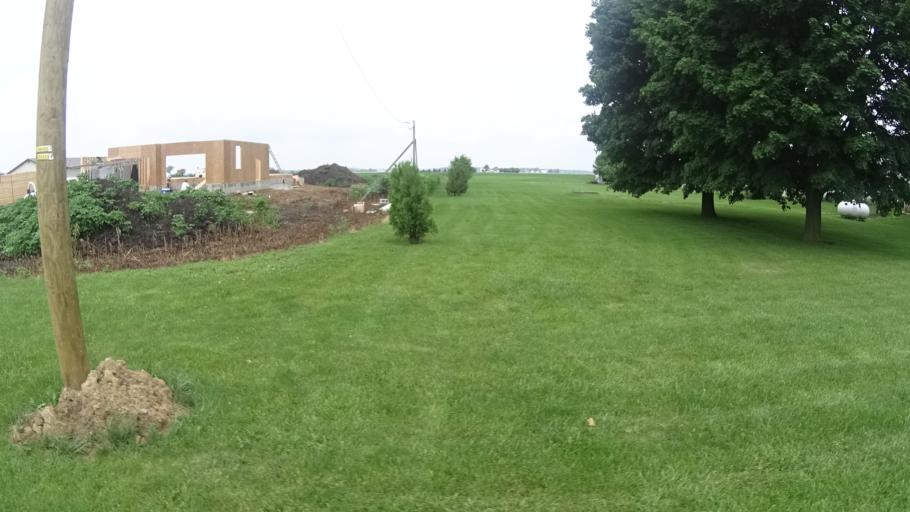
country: US
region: Ohio
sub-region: Huron County
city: Bellevue
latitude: 41.2946
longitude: -82.8073
